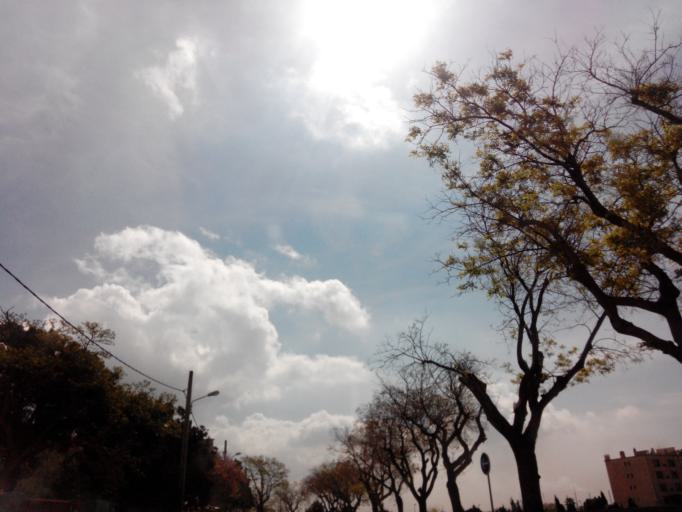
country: FR
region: Provence-Alpes-Cote d'Azur
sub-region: Departement des Bouches-du-Rhone
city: Port-de-Bouc
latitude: 43.4086
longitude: 4.9798
